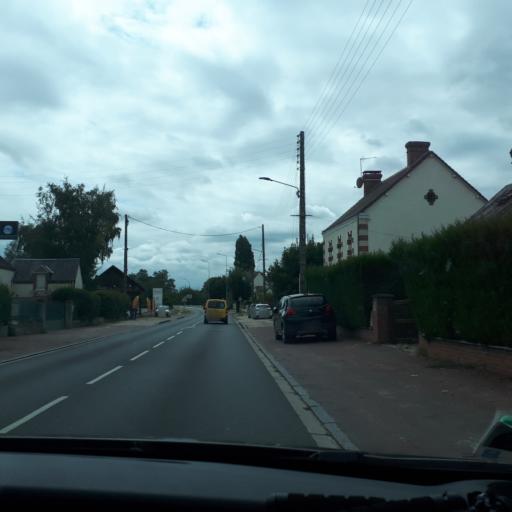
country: FR
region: Centre
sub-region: Departement du Loiret
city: Saint-Pere-sur-Loire
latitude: 47.7742
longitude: 2.3723
